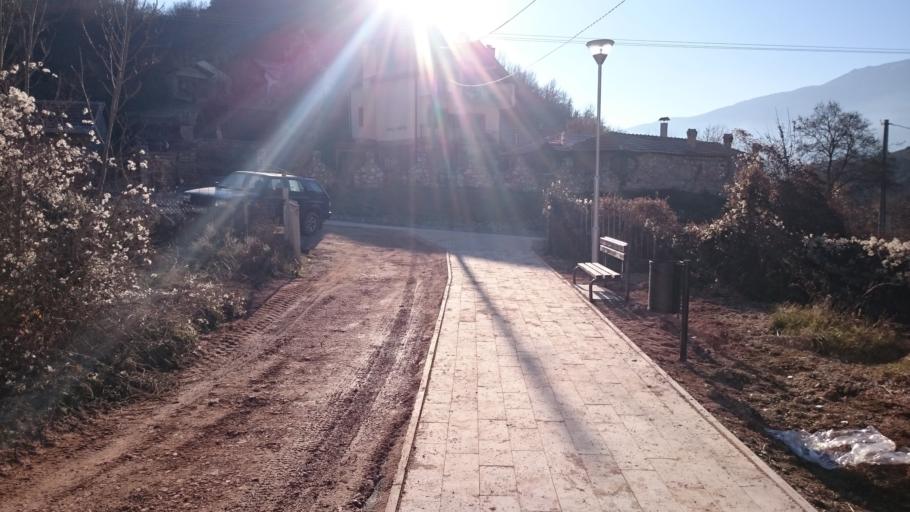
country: MK
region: Makedonski Brod
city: Makedonski Brod
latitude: 41.5457
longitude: 21.2498
